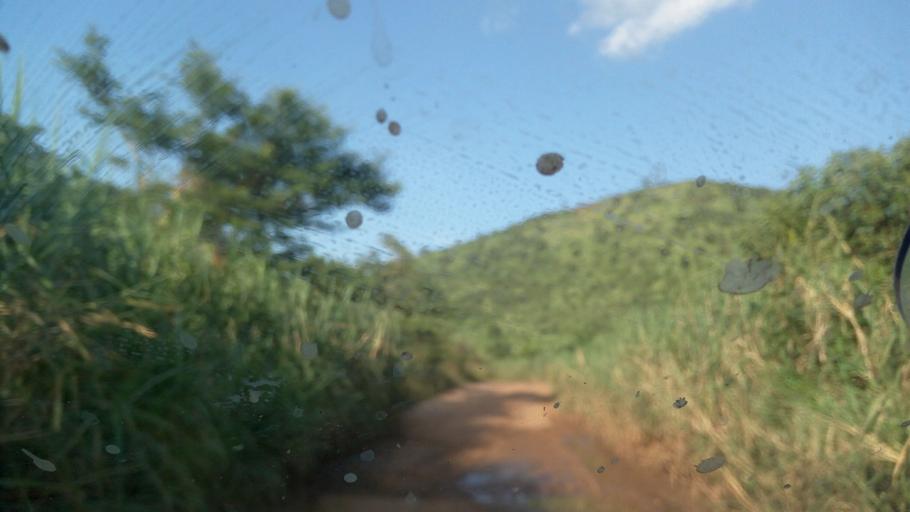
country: BI
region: Bururi
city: Rumonge
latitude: -4.2148
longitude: 28.9996
